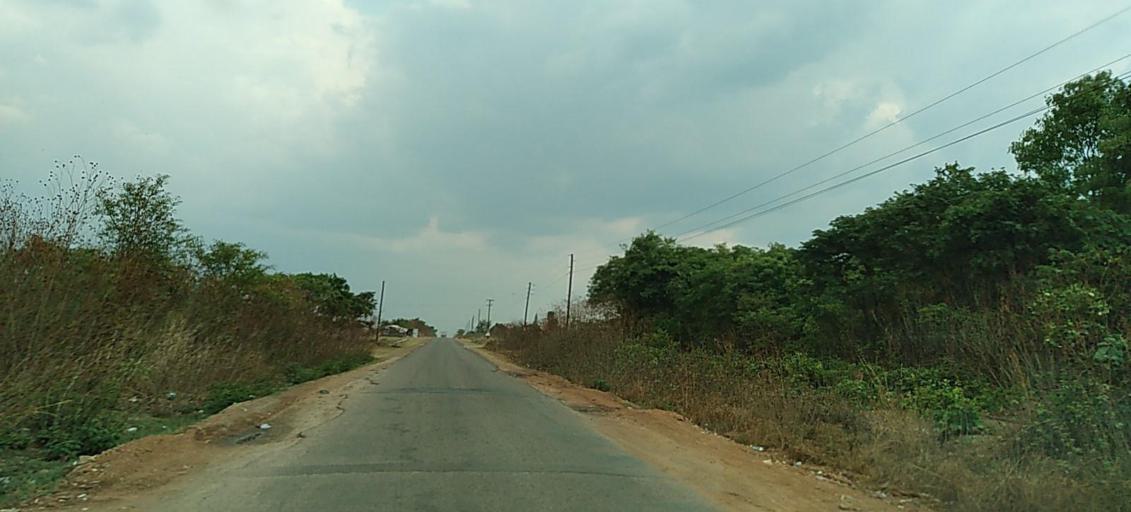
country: ZM
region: Copperbelt
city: Kalulushi
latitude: -12.8570
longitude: 28.1223
